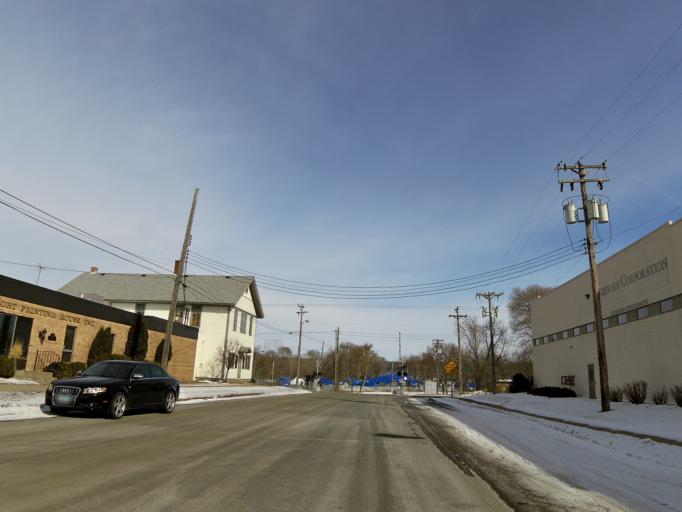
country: US
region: Minnesota
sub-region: Washington County
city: Bayport
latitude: 45.0169
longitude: -92.7771
